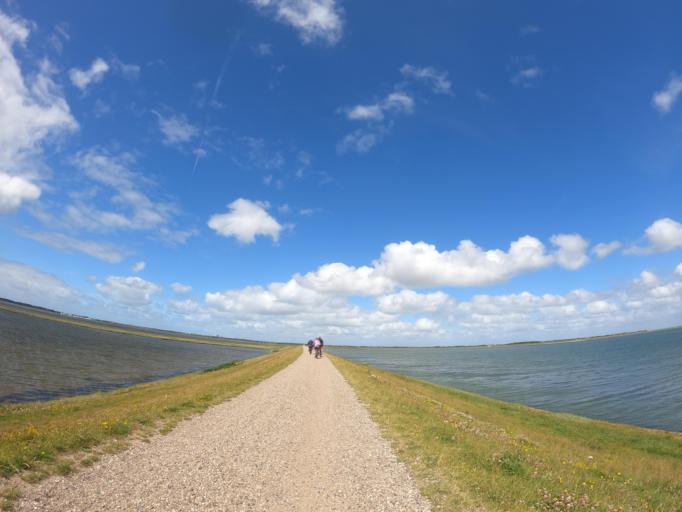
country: DE
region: Schleswig-Holstein
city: Tinnum
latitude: 54.8666
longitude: 8.3335
